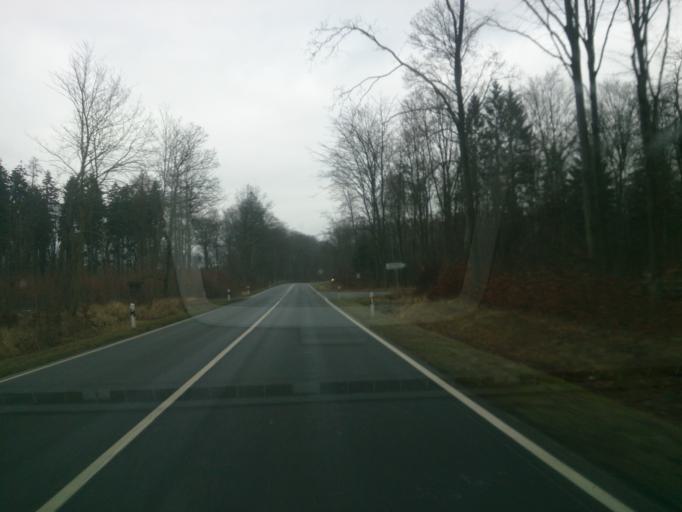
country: DE
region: Mecklenburg-Vorpommern
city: Borrentin
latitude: 53.7475
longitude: 12.9295
